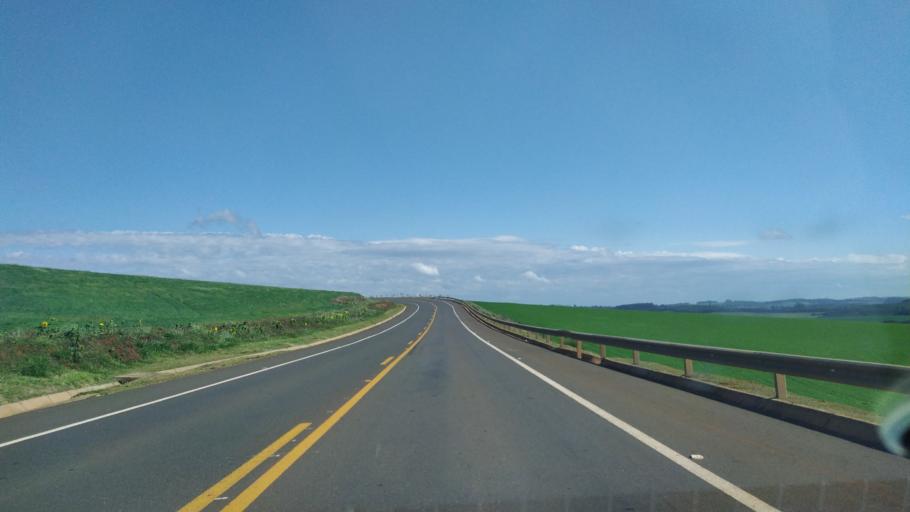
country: BR
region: Parana
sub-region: Ortigueira
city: Ortigueira
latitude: -24.2573
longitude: -50.8075
